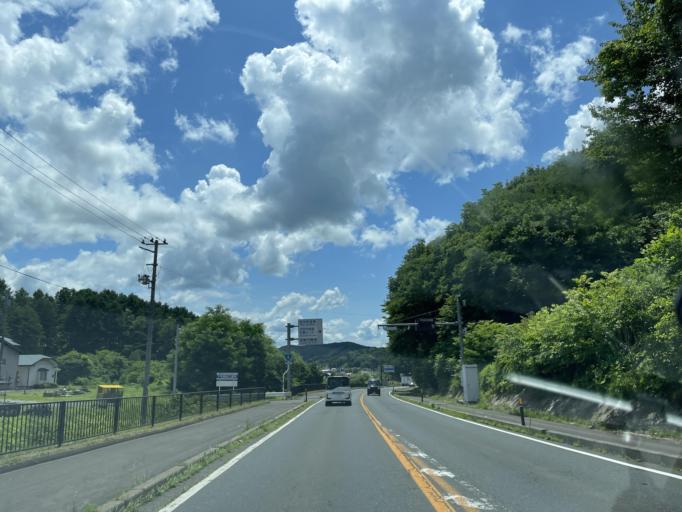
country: JP
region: Iwate
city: Ichinohe
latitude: 39.9716
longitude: 141.2142
